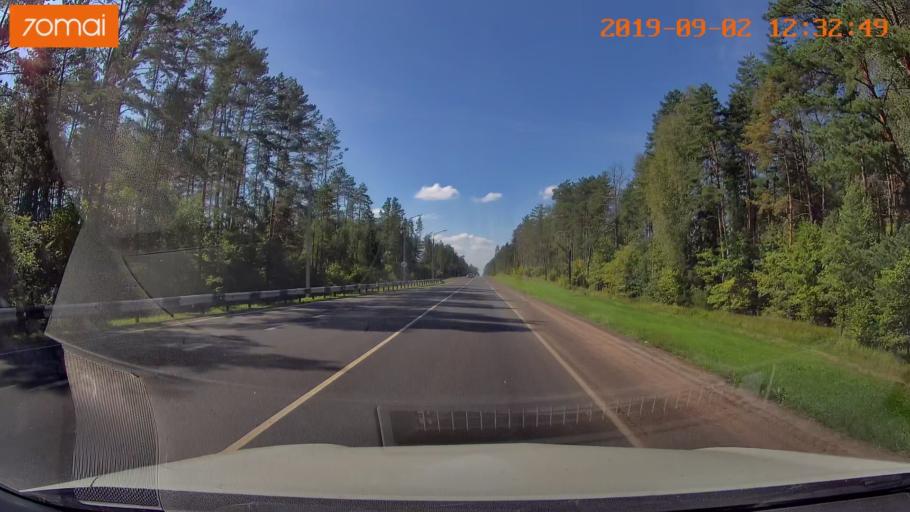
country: RU
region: Smolensk
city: Shumyachi
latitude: 53.8220
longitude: 32.4417
